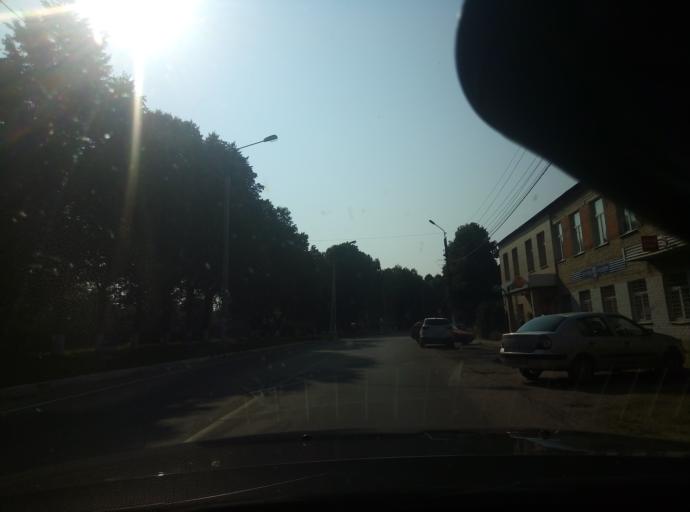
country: RU
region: Kaluga
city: Zhukovo
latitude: 55.0300
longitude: 36.7476
